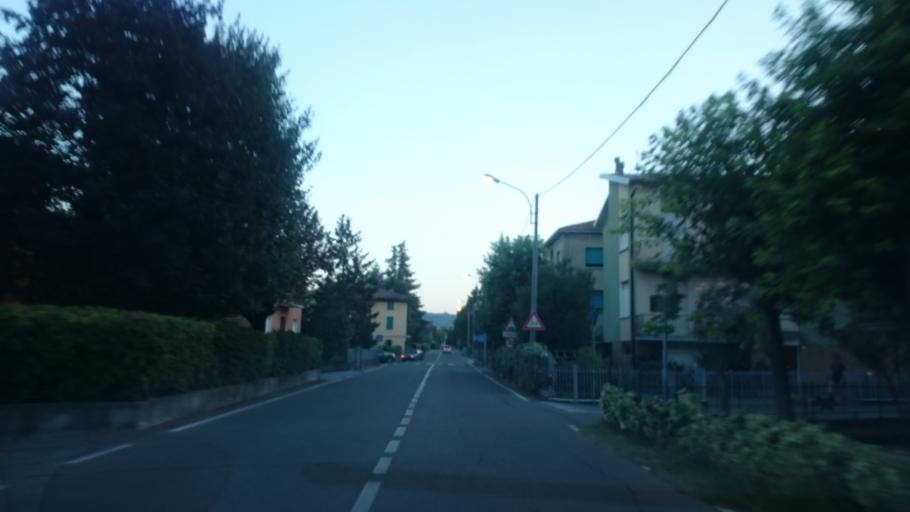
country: IT
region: Emilia-Romagna
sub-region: Provincia di Reggio Emilia
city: Arceto
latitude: 44.6187
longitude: 10.7211
